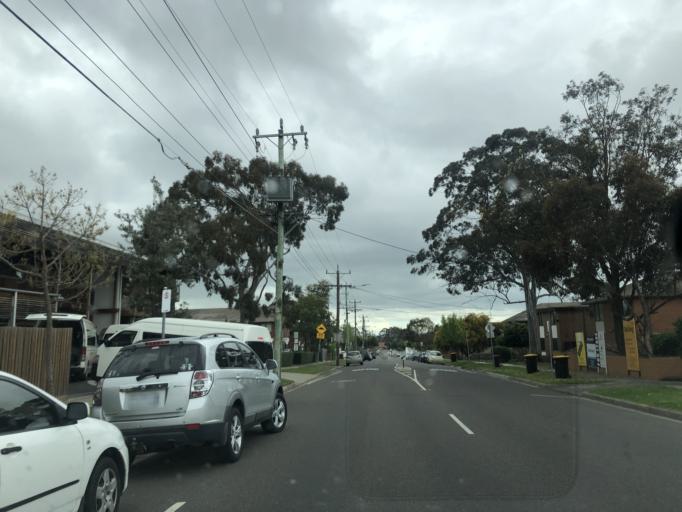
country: AU
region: Victoria
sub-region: Greater Dandenong
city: Dandenong
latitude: -37.9813
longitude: 145.2063
